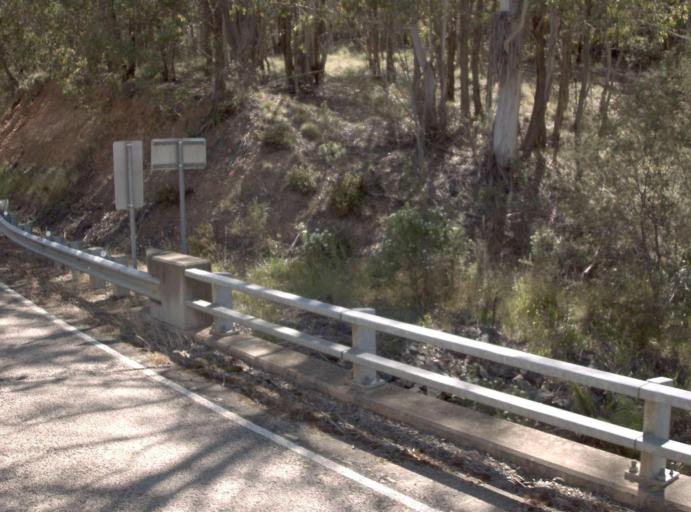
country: AU
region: New South Wales
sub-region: Bombala
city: Bombala
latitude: -37.1640
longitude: 148.7179
